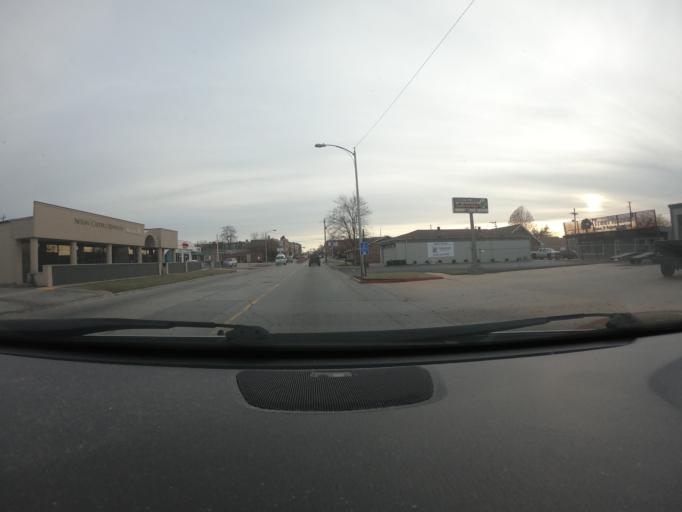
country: US
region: Arkansas
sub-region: Benton County
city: Rogers
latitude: 36.3351
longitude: -94.1172
